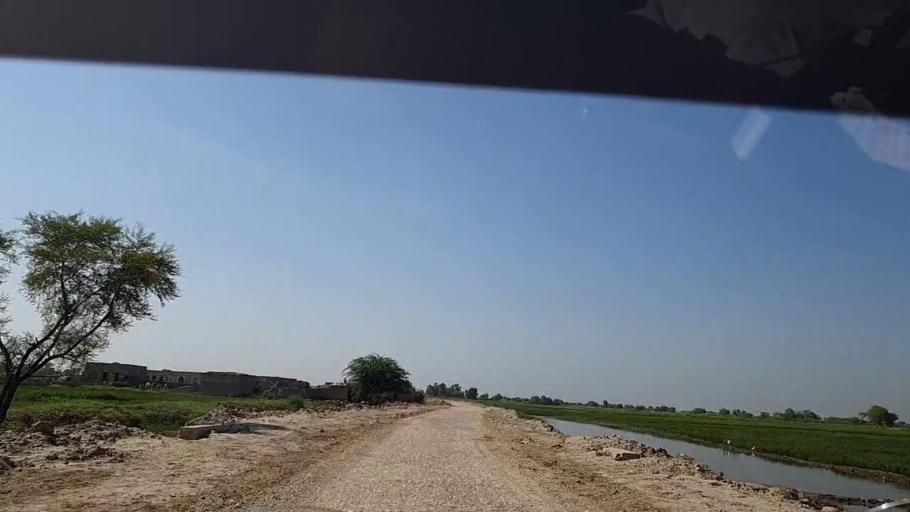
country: PK
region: Sindh
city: Tangwani
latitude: 28.3290
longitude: 69.0773
